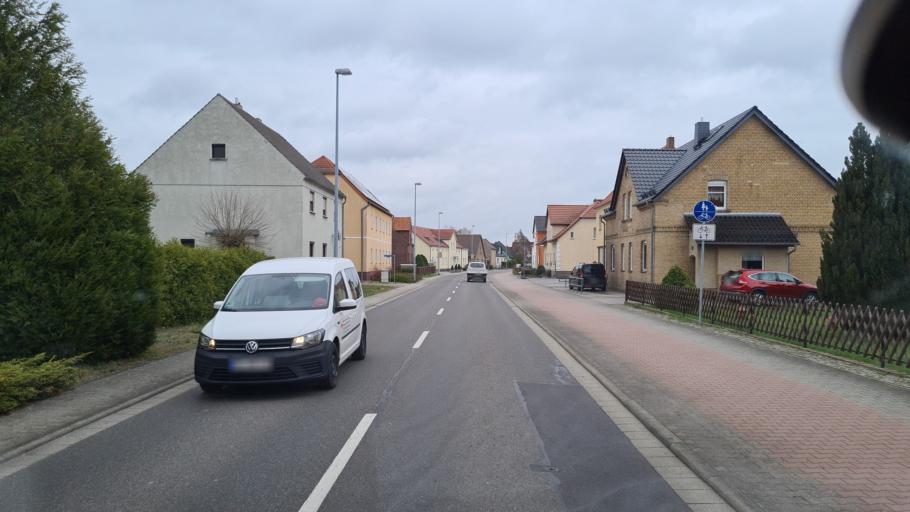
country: DE
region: Brandenburg
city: Schwarzheide
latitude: 51.4889
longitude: 13.8291
